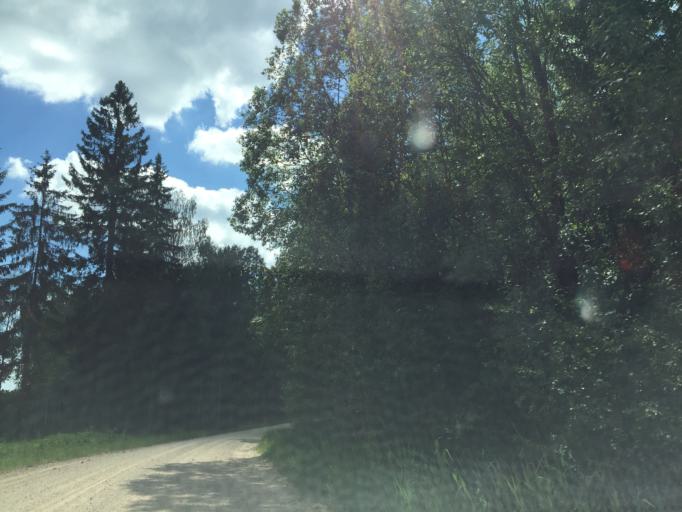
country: LV
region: Priekuli
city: Priekuli
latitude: 57.2323
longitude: 25.4396
